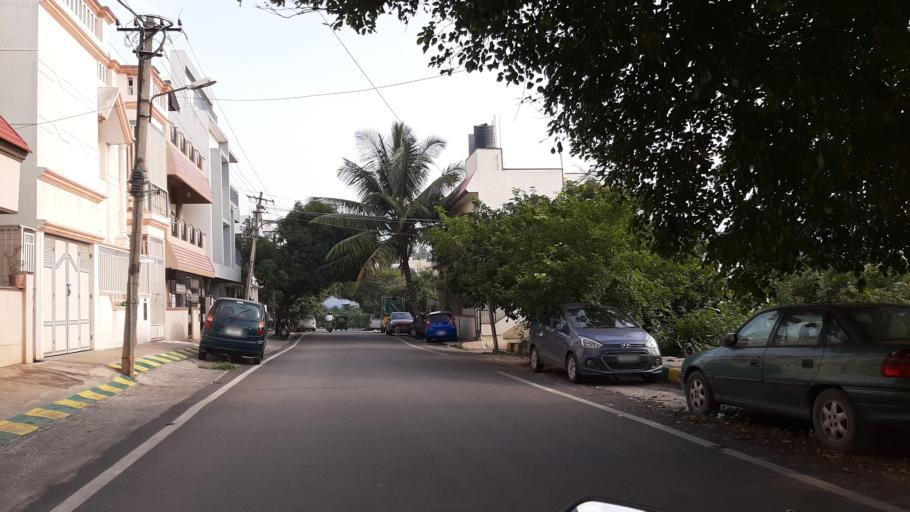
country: IN
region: Karnataka
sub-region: Bangalore Urban
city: Bangalore
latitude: 12.9752
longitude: 77.5126
